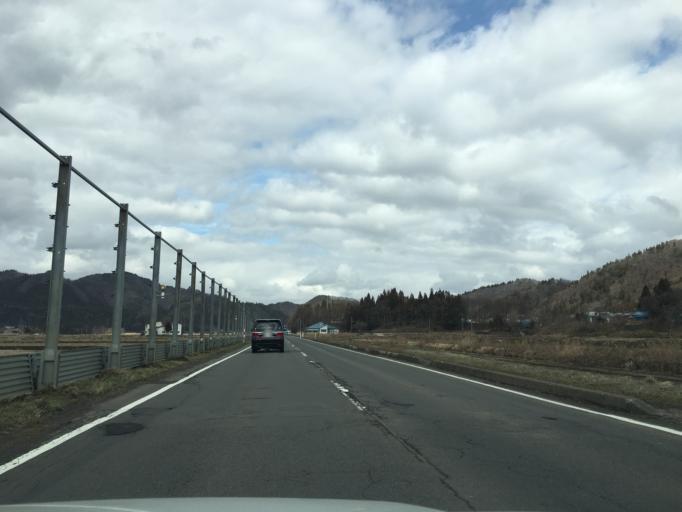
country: JP
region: Akita
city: Hanawa
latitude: 40.2326
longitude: 140.7337
